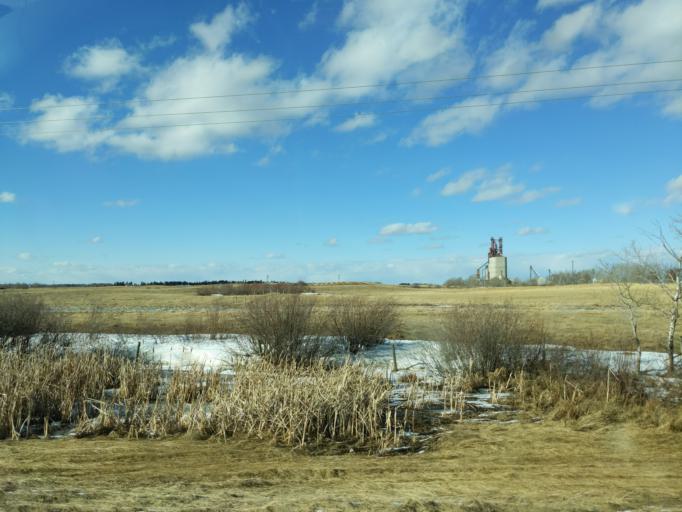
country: CA
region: Saskatchewan
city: Lloydminster
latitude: 53.2489
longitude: -109.9688
